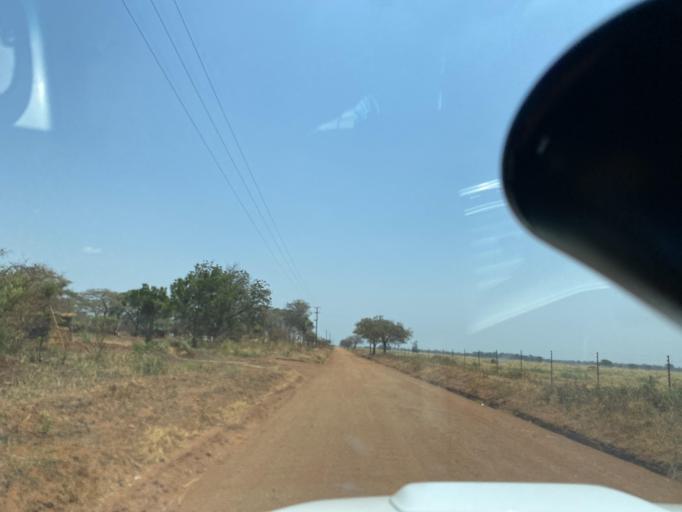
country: ZM
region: Lusaka
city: Lusaka
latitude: -15.4401
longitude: 28.0587
